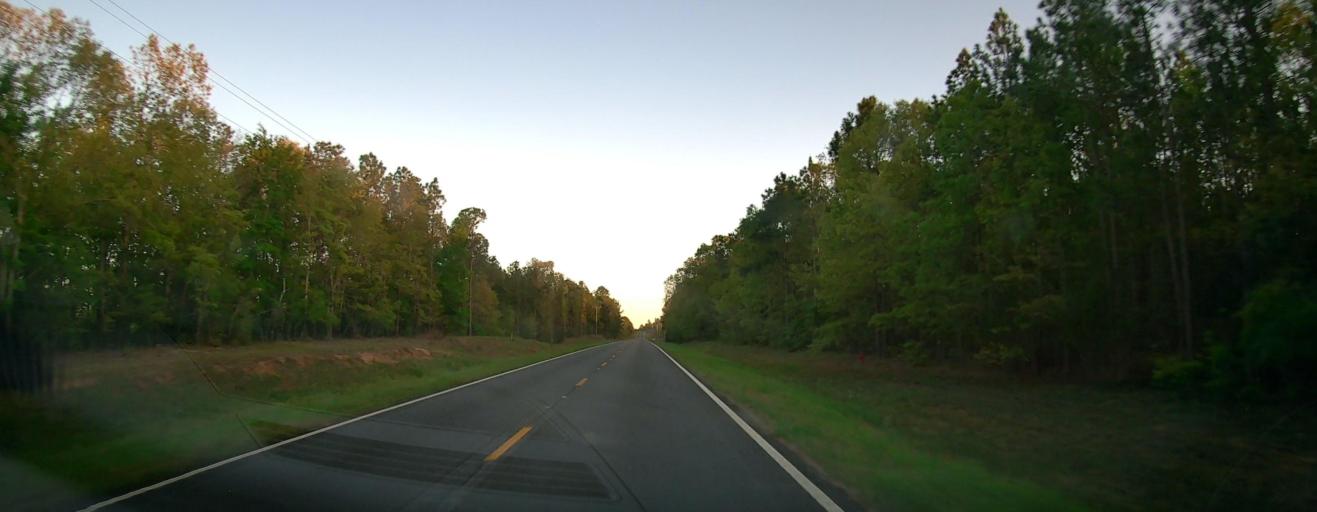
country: US
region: Georgia
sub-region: Marion County
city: Buena Vista
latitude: 32.4129
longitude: -84.5852
